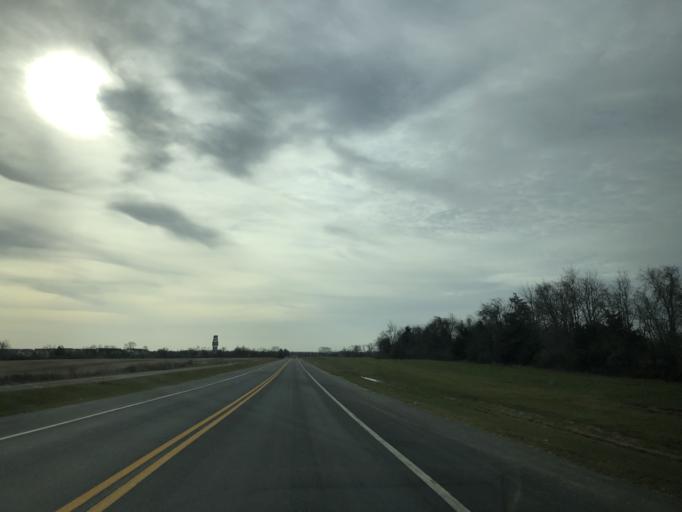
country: US
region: Delaware
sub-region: New Castle County
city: Middletown
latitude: 39.5212
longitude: -75.6794
